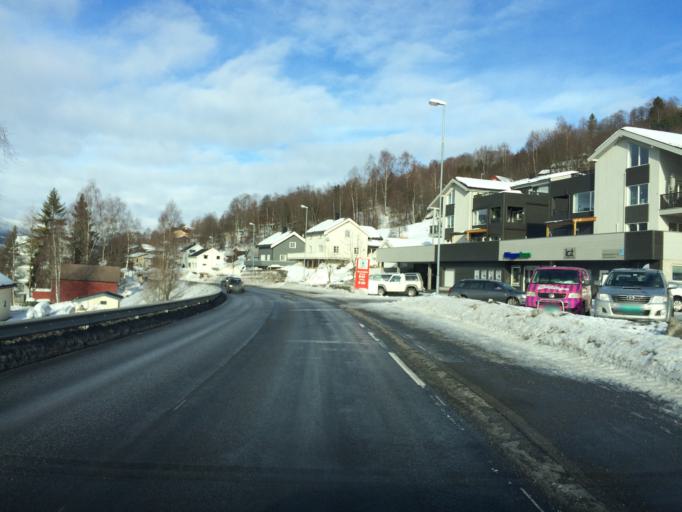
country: NO
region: Oppland
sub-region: Gausdal
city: Segalstad bru
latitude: 61.2262
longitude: 10.2273
